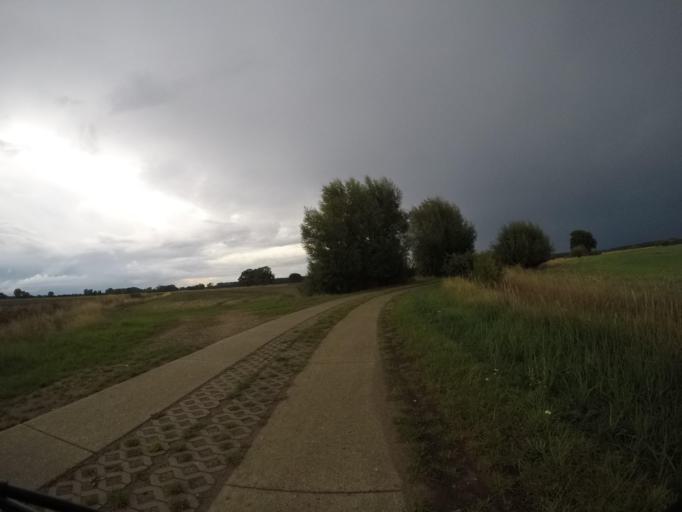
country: DE
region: Lower Saxony
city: Neu Darchau
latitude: 53.2574
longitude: 10.8869
